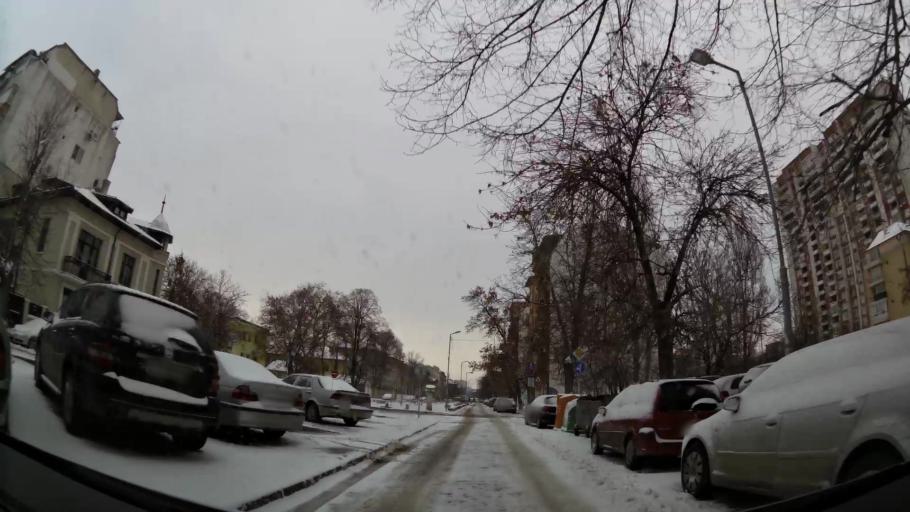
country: BG
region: Sofia-Capital
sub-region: Stolichna Obshtina
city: Sofia
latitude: 42.6980
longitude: 23.2998
